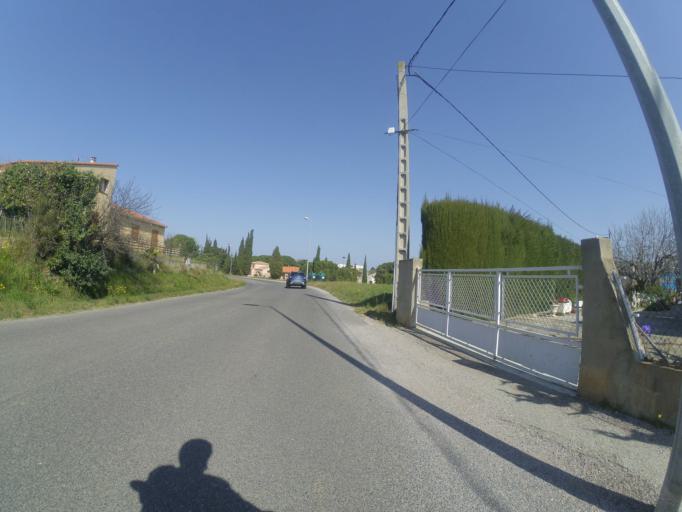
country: FR
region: Languedoc-Roussillon
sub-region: Departement des Pyrenees-Orientales
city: Llupia
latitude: 42.6268
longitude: 2.7621
